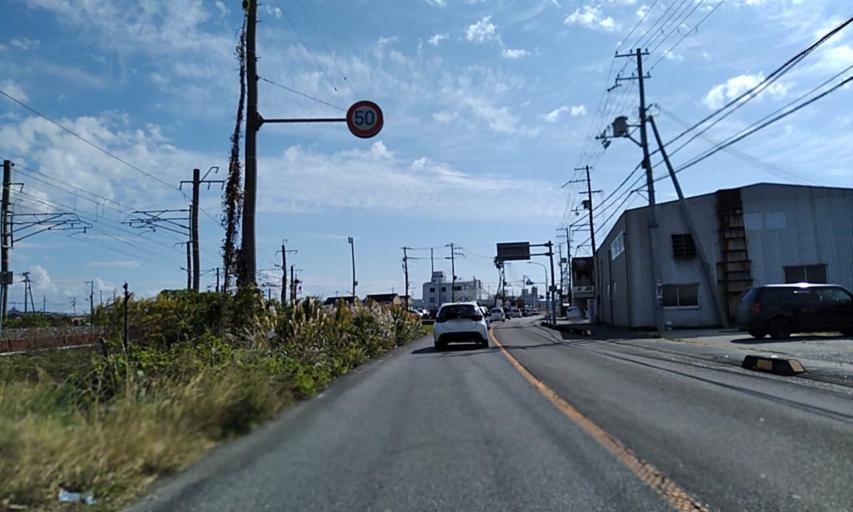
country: JP
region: Wakayama
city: Gobo
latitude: 33.9089
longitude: 135.1506
